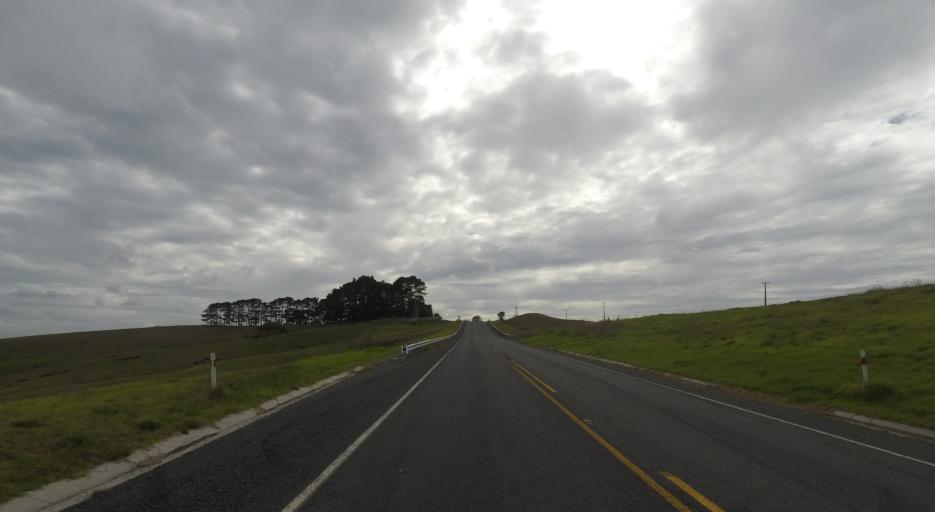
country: NZ
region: Auckland
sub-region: Auckland
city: Rothesay Bay
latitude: -36.6582
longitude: 174.6843
